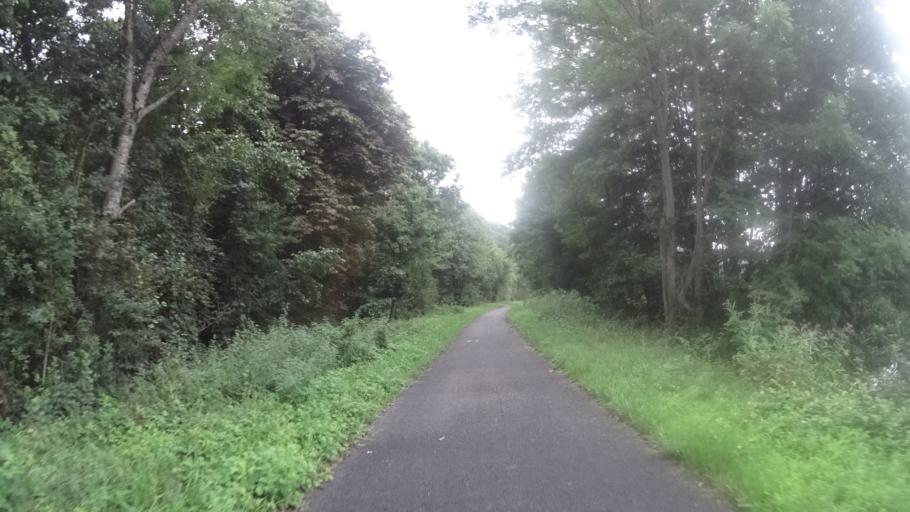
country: FR
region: Lorraine
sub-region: Departement de Meurthe-et-Moselle
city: Velaine-en-Haye
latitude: 48.6600
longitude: 6.0067
